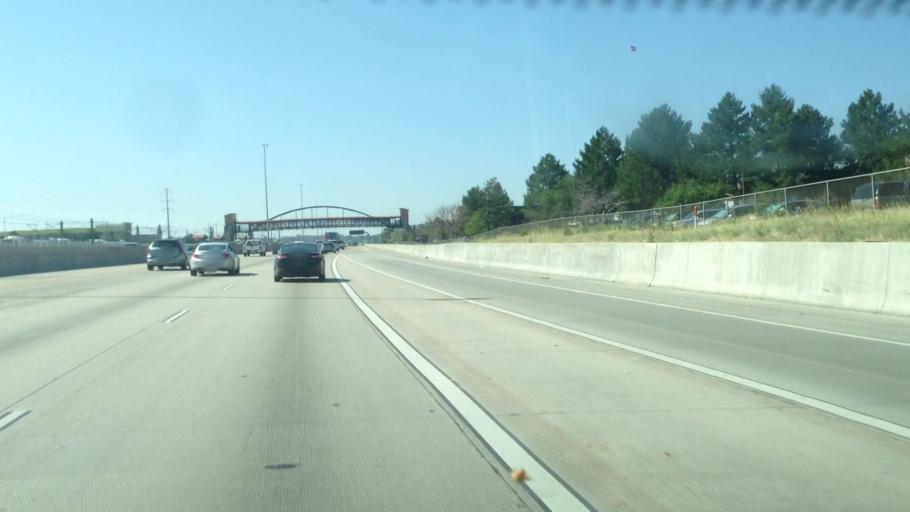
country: US
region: Colorado
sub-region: Adams County
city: Aurora
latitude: 39.6935
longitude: -104.8292
